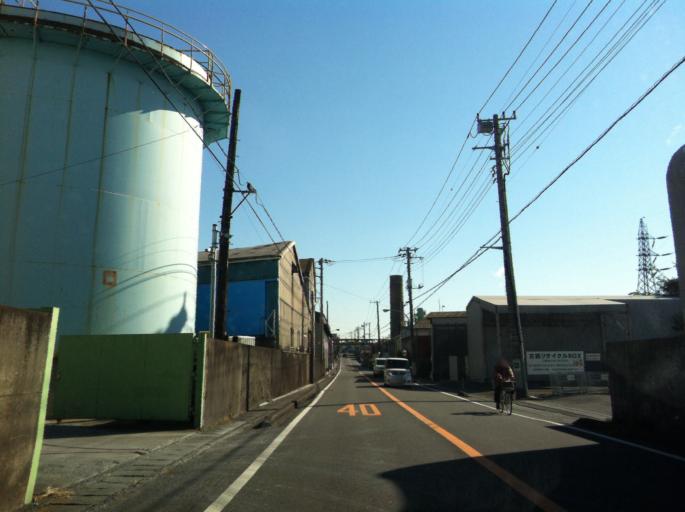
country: JP
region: Shizuoka
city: Fuji
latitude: 35.1660
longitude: 138.7091
